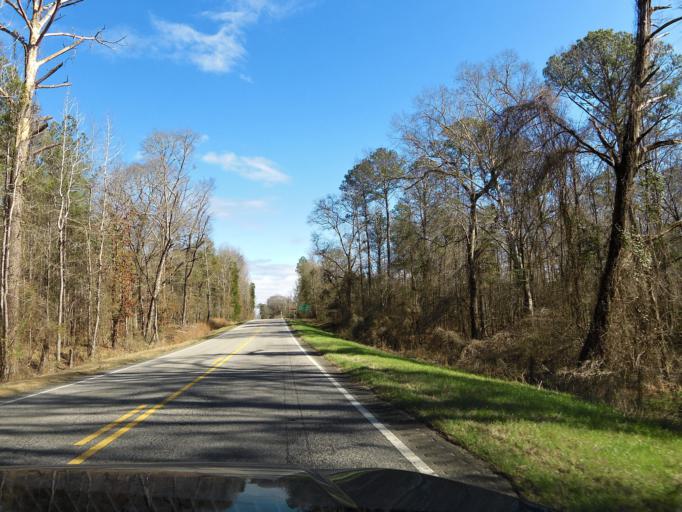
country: US
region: Alabama
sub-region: Barbour County
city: Clayton
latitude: 32.0345
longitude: -85.3860
